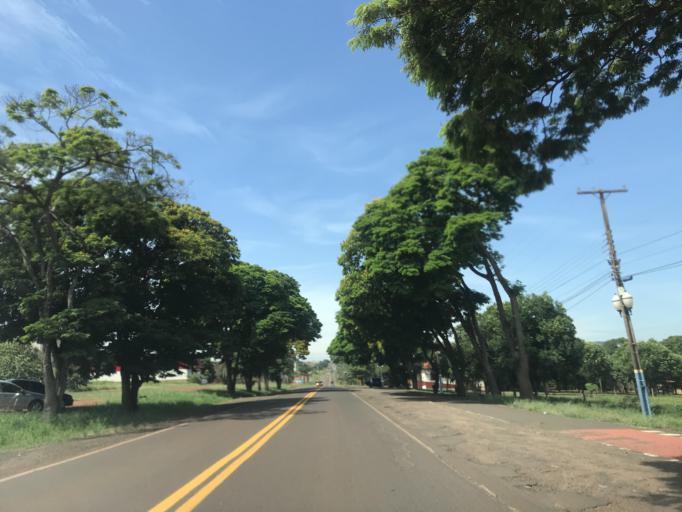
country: BR
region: Parana
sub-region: Terra Rica
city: Terra Rica
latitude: -22.7362
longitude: -52.6246
